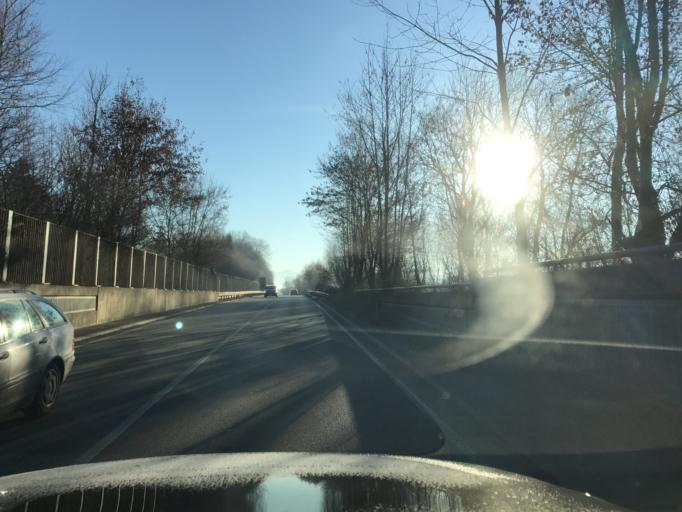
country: DE
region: Bavaria
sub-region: Upper Bavaria
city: Bad Aibling
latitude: 47.8558
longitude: 11.9933
